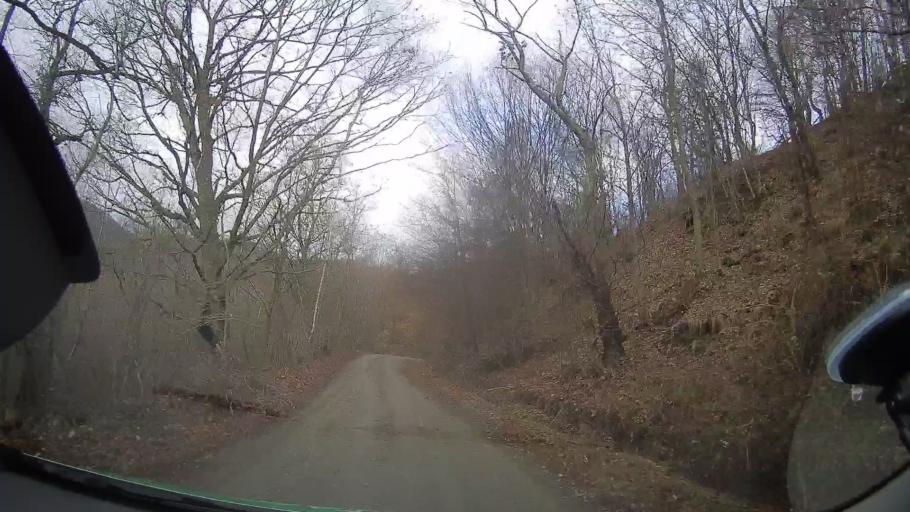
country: RO
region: Cluj
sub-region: Comuna Valea Ierii
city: Valea Ierii
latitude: 46.6479
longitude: 23.3497
